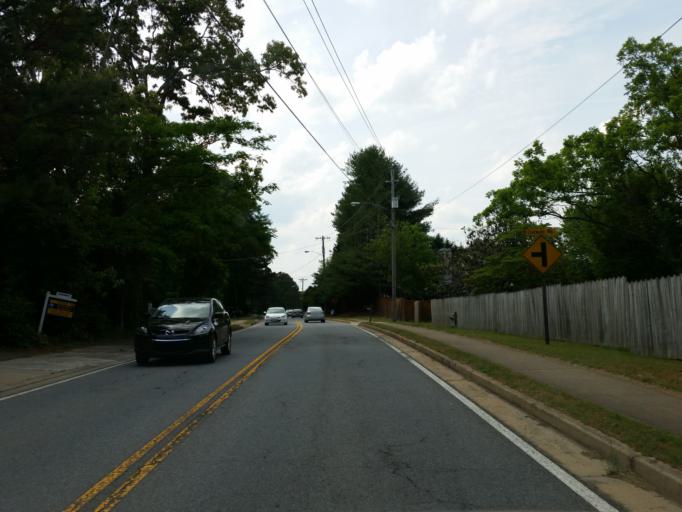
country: US
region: Georgia
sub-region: Cobb County
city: Marietta
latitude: 33.9939
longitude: -84.4681
